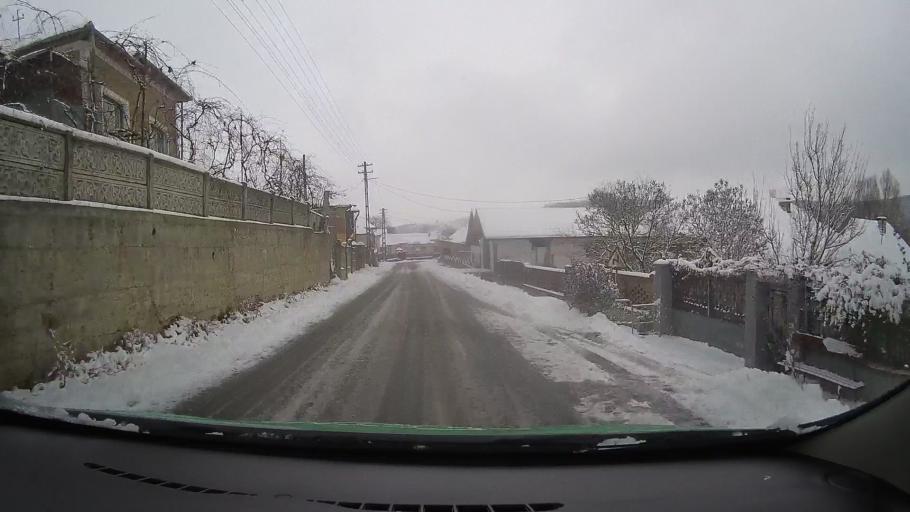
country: RO
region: Hunedoara
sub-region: Comuna Pestisu Mic
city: Pestisu Mic
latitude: 45.8182
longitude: 22.8898
